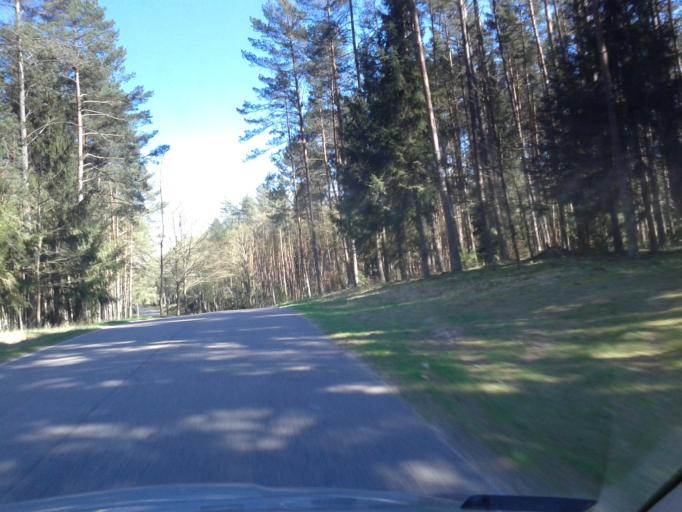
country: PL
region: West Pomeranian Voivodeship
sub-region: Powiat szczecinecki
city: Lubowo
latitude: 53.6341
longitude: 16.3357
